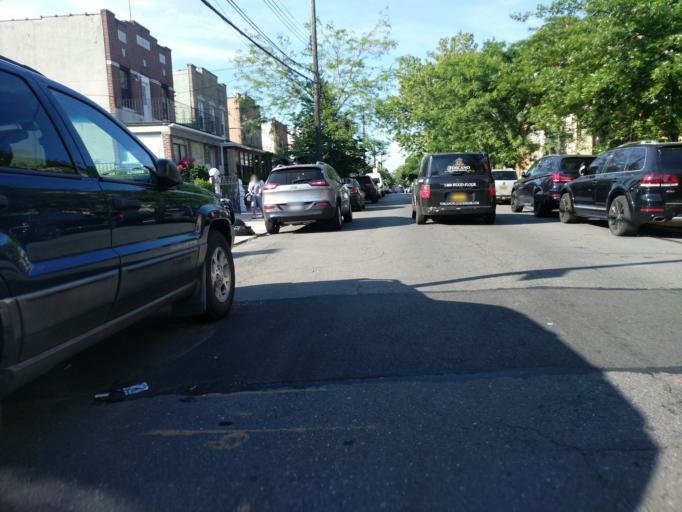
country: US
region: New York
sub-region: Queens County
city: Long Island City
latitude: 40.7561
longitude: -73.9180
